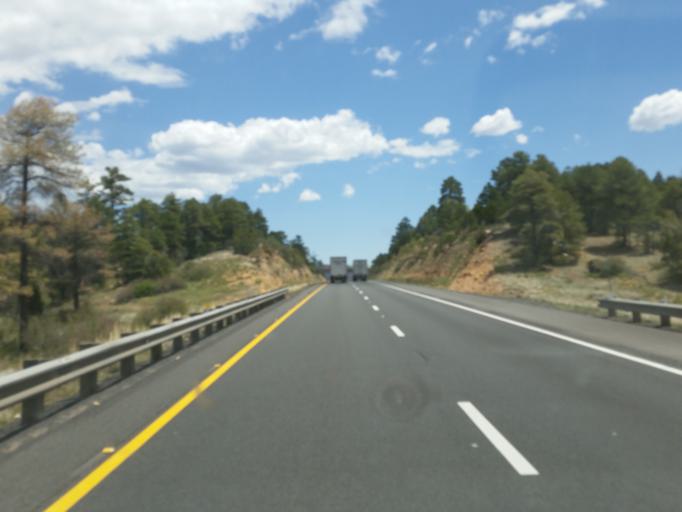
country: US
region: Arizona
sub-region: Coconino County
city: Flagstaff
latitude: 35.1990
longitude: -111.6116
